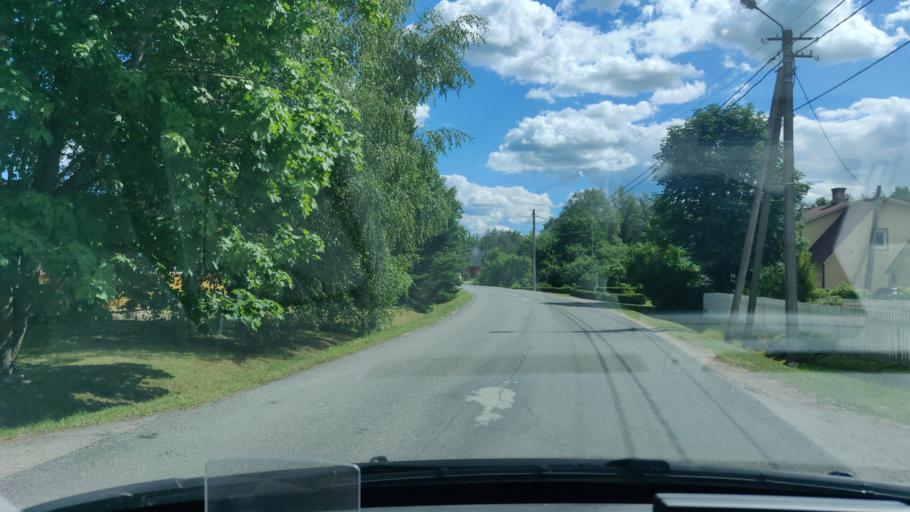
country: EE
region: Jogevamaa
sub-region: Mustvee linn
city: Mustvee
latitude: 58.9843
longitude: 26.8627
